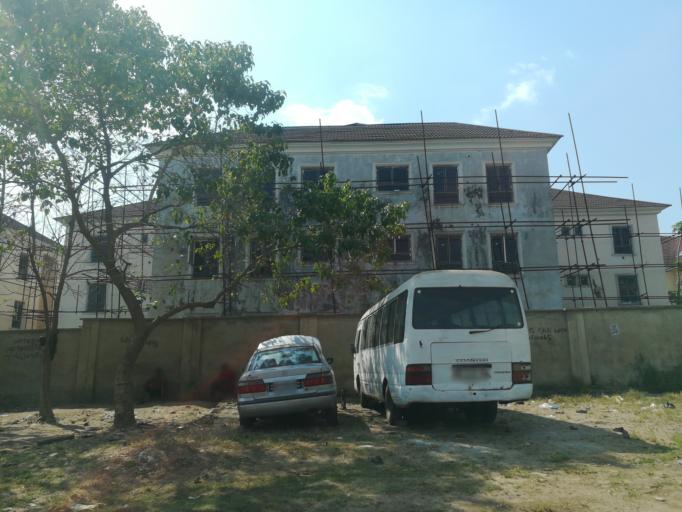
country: NG
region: Abuja Federal Capital Territory
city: Abuja
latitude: 9.0627
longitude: 7.4300
